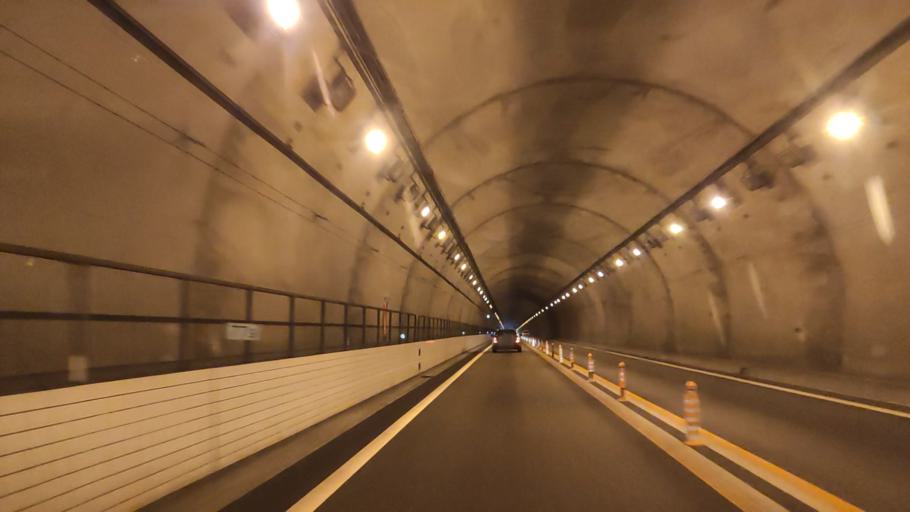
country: JP
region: Tokushima
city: Ikedacho
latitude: 34.0223
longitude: 133.7982
